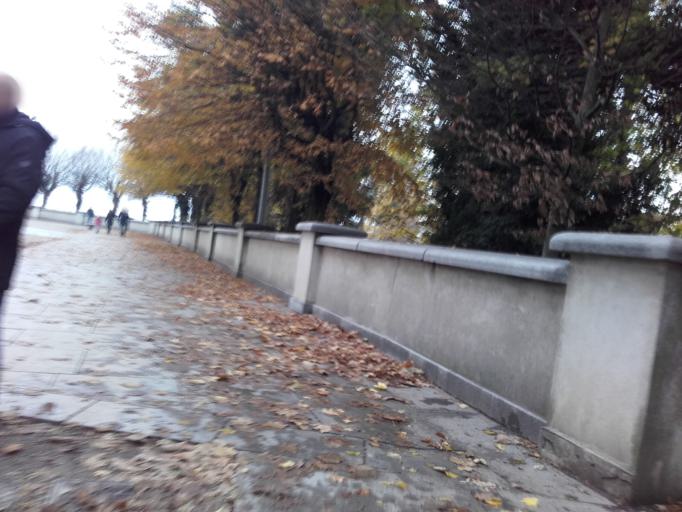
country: IT
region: Piedmont
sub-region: Provincia di Torino
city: San Mauro Torinese
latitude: 45.0812
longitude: 7.7676
